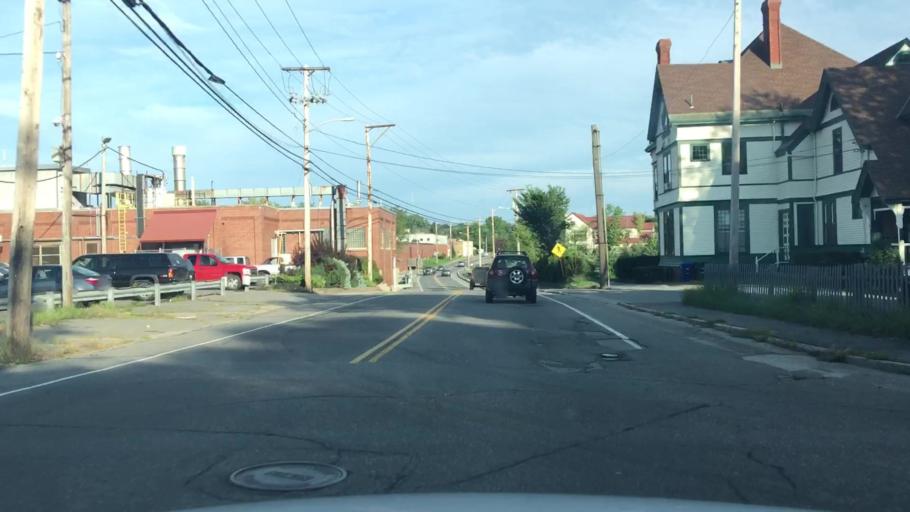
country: US
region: Maine
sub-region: Cumberland County
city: Westbrook
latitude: 43.6836
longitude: -70.3537
